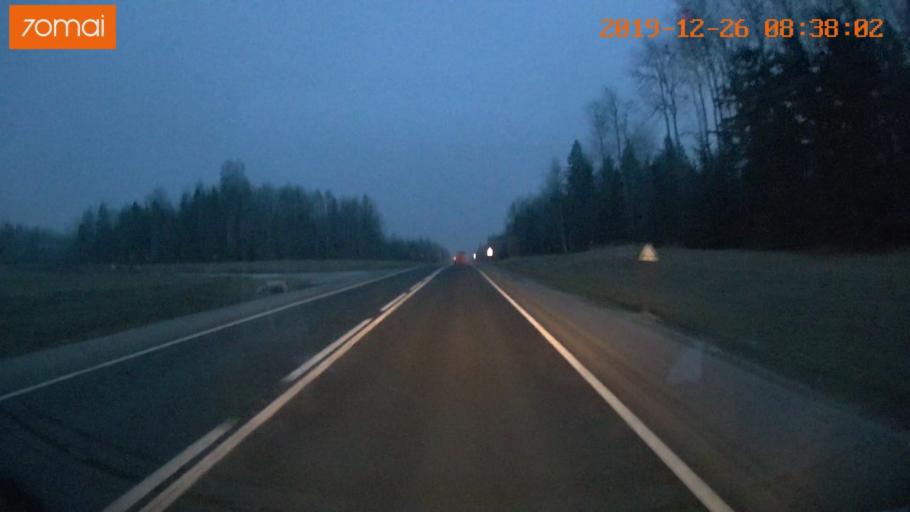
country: RU
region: Jaroslavl
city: Prechistoye
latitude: 58.5099
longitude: 40.3453
